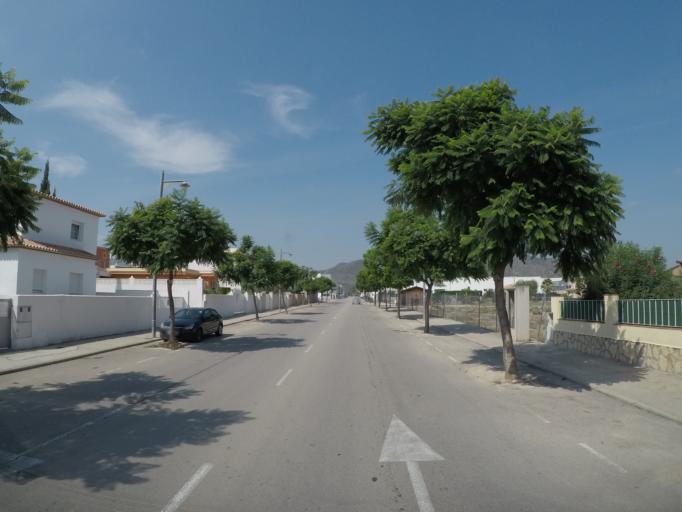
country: ES
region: Valencia
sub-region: Provincia de Alicante
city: Pego
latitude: 38.8455
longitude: -0.1104
